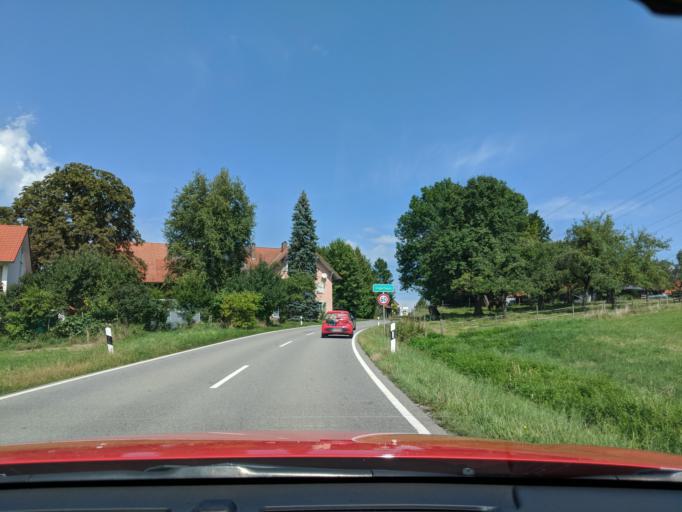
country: DE
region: Baden-Wuerttemberg
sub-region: Tuebingen Region
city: Wangen im Allgau
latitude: 47.7253
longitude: 9.8196
